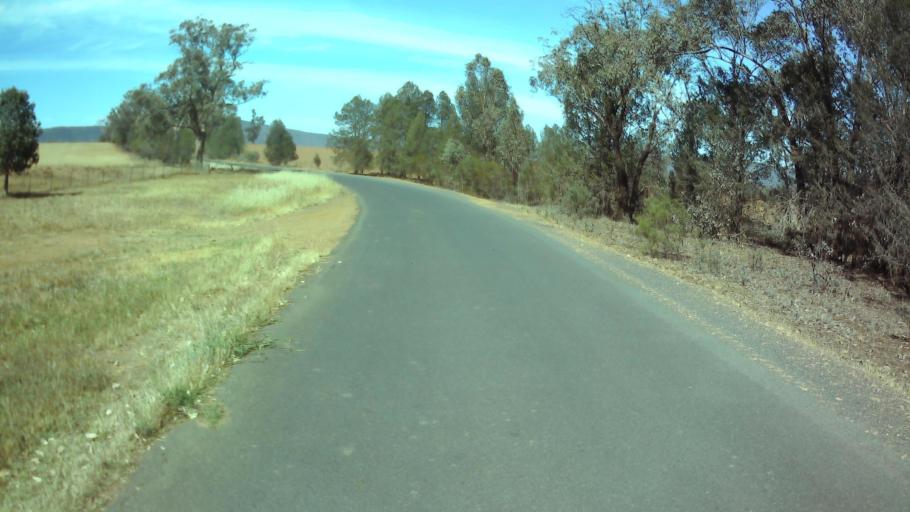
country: AU
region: New South Wales
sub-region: Weddin
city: Grenfell
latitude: -33.9317
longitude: 148.0854
